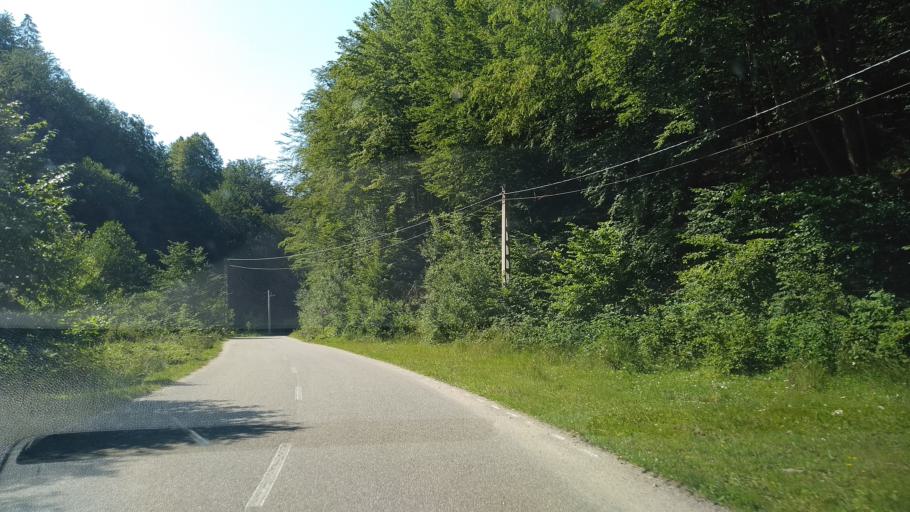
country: RO
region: Hunedoara
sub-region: Comuna Orastioara de Sus
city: Orastioara de Sus
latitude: 45.6296
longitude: 23.2180
